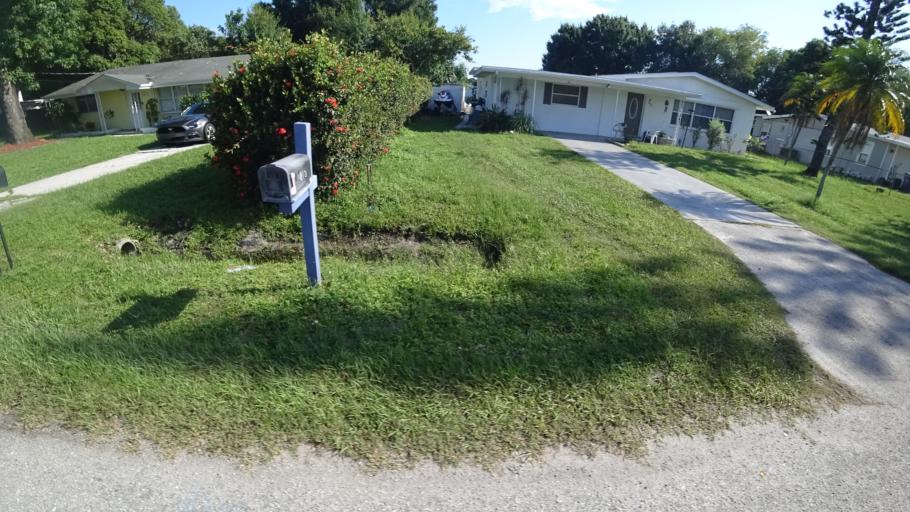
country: US
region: Florida
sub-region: Manatee County
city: South Bradenton
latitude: 27.4647
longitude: -82.5727
